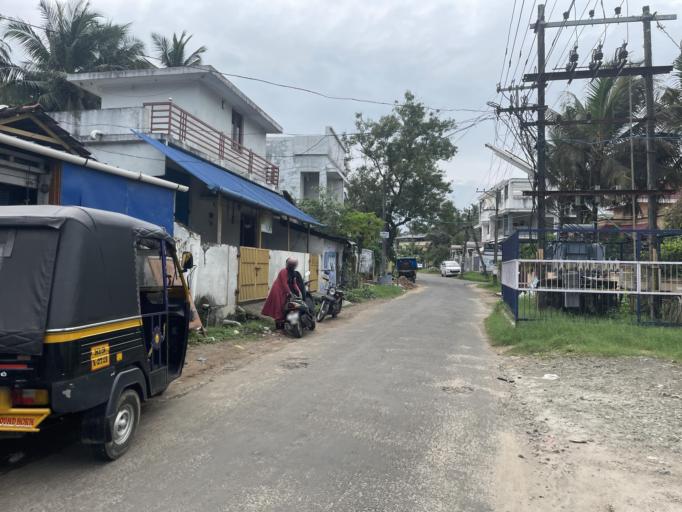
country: IN
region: Kerala
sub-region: Palakkad district
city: Chittur
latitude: 10.6946
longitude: 76.7391
